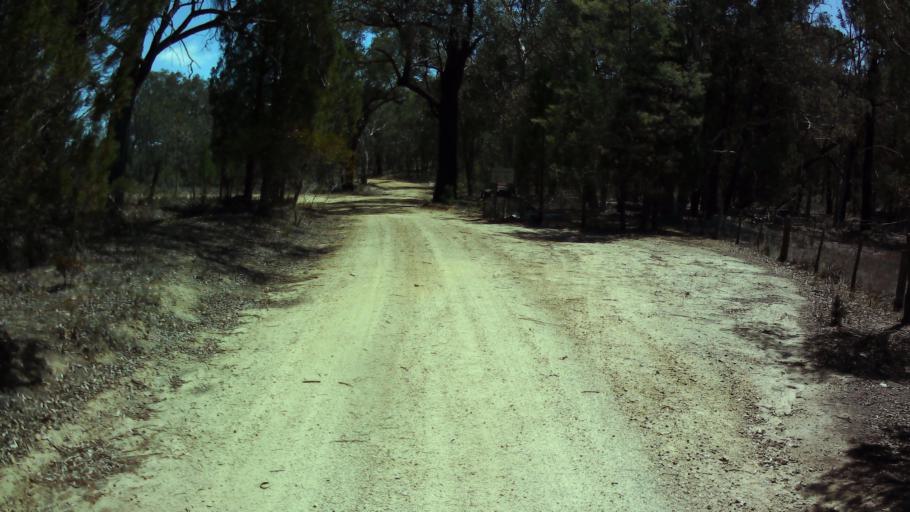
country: AU
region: New South Wales
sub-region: Cowra
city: Cowra
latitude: -33.8373
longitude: 148.4522
